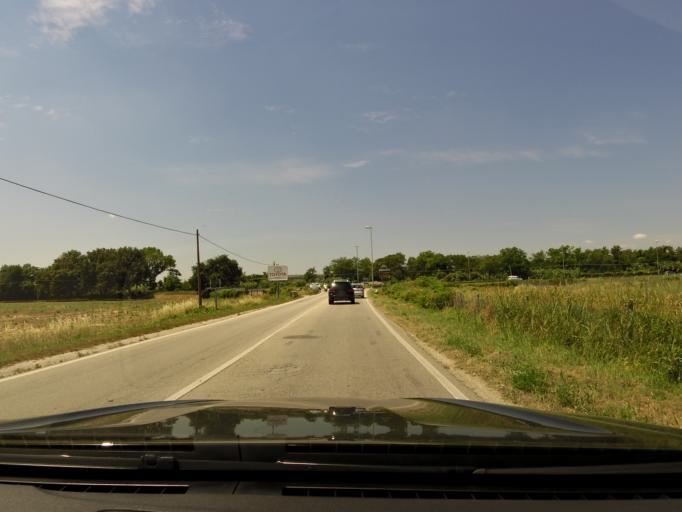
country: IT
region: The Marches
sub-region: Provincia di Pesaro e Urbino
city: Rosciano
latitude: 43.8186
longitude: 13.0192
